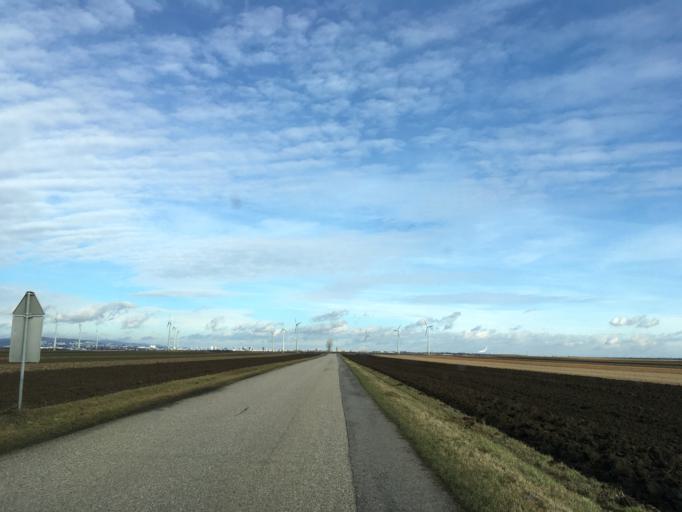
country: AT
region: Burgenland
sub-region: Politischer Bezirk Neusiedl am See
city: Pama
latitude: 48.0541
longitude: 17.0330
